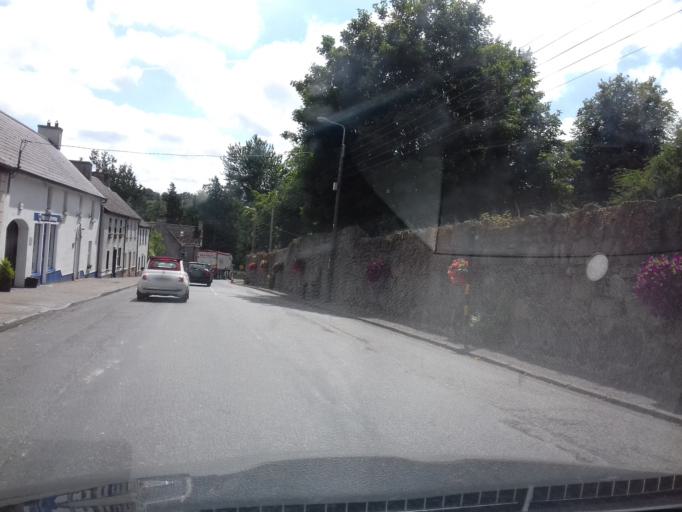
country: IE
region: Leinster
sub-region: Kilkenny
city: Graiguenamanagh
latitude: 52.5982
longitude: -6.9206
